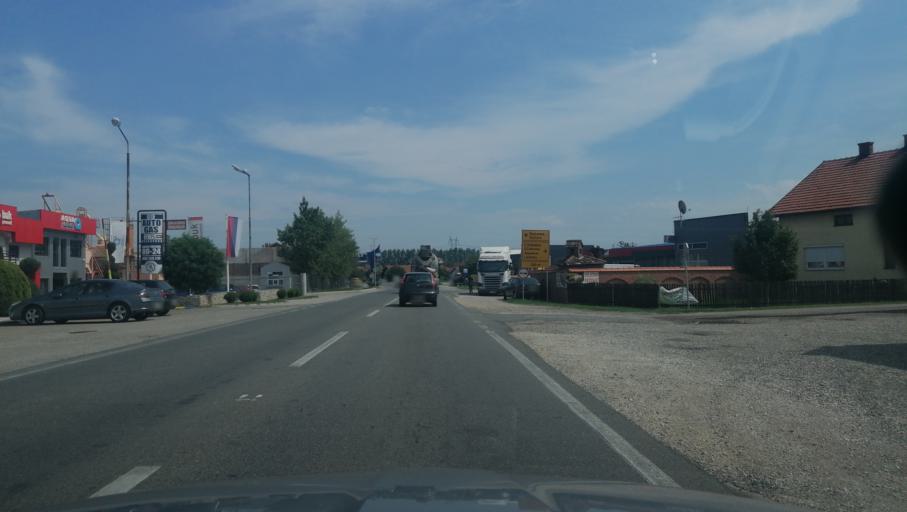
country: BA
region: Republika Srpska
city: Velika Obarska
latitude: 44.7678
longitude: 19.1649
